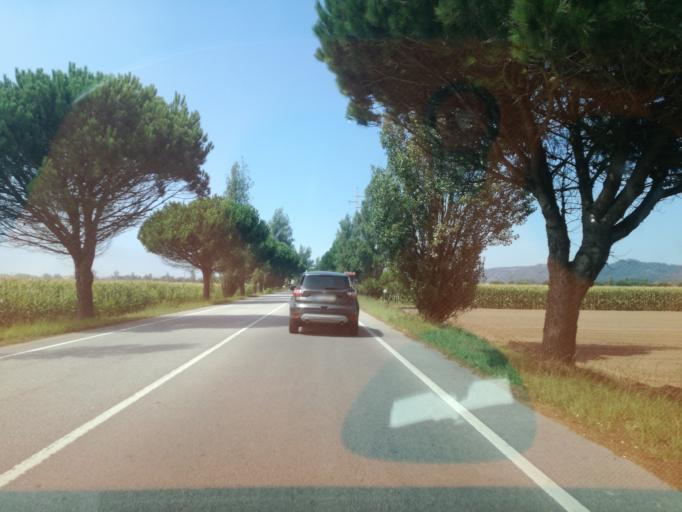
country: PT
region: Braga
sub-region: Esposende
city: Esposende
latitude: 41.5213
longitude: -8.7714
